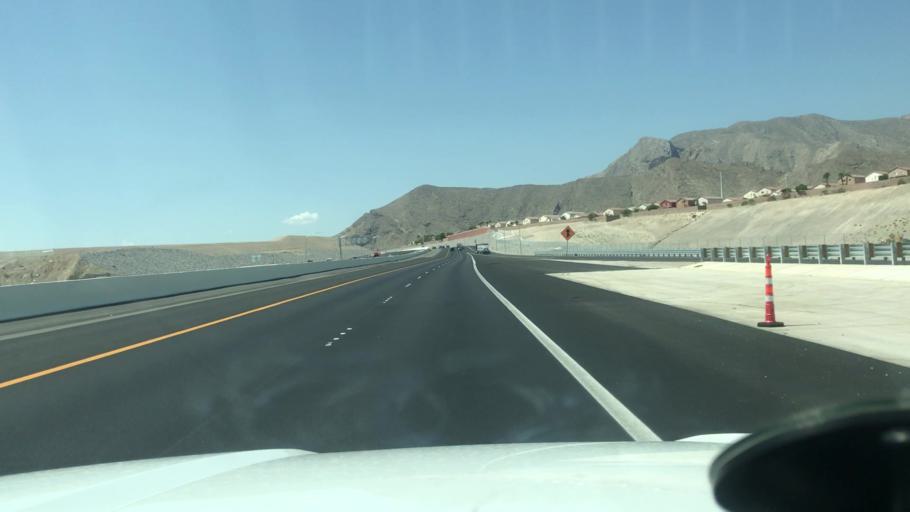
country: US
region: Nevada
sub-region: Clark County
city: Summerlin South
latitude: 36.2456
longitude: -115.3200
